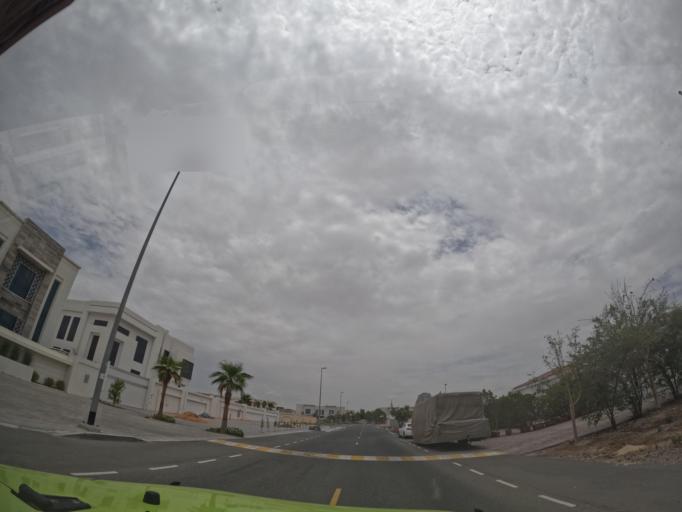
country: AE
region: Ash Shariqah
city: Sharjah
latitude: 25.1325
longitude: 55.3698
